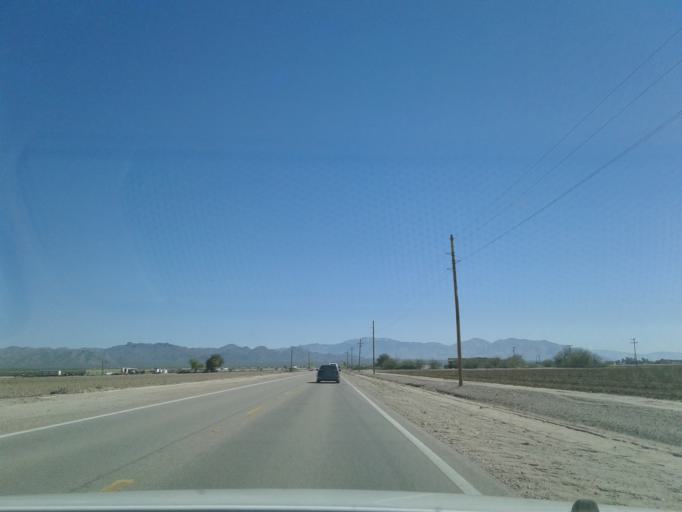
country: US
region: Arizona
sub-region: Pima County
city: Marana
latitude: 32.4605
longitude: -111.2386
